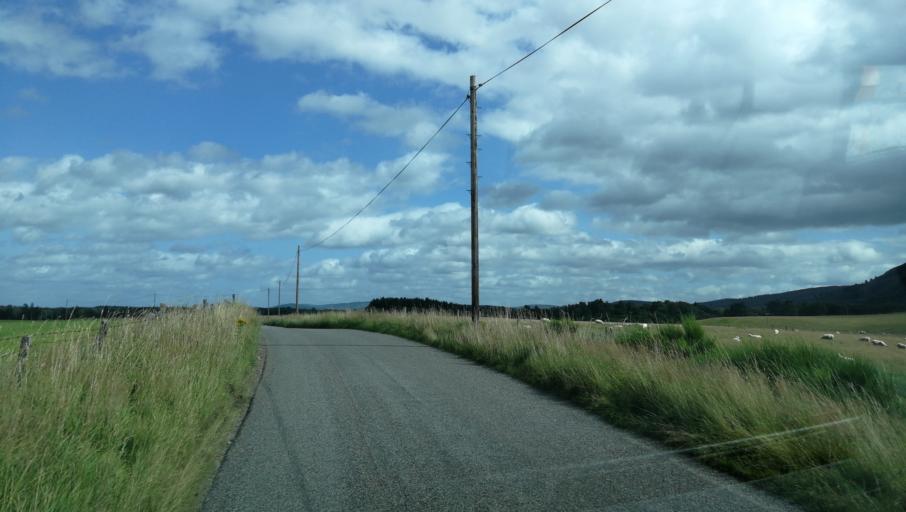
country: GB
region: Scotland
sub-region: Highland
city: Aviemore
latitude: 57.2101
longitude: -3.7751
